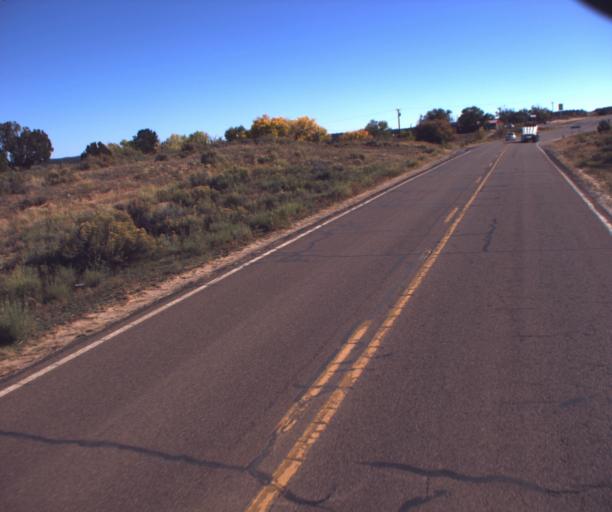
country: US
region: Arizona
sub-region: Apache County
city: Ganado
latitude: 35.5040
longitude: -109.5279
